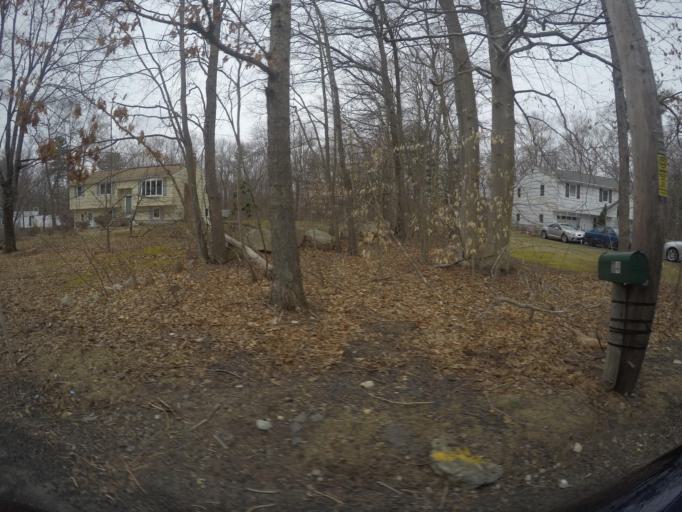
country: US
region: Massachusetts
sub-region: Bristol County
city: Easton
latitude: 42.0556
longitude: -71.1424
